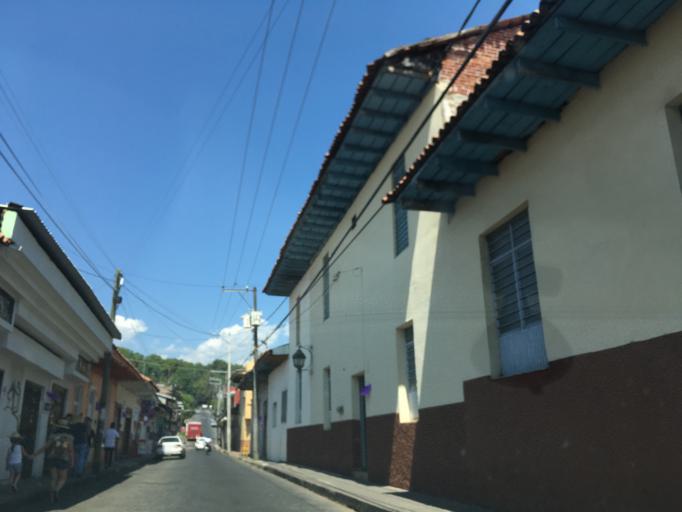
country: MX
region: Michoacan
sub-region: Uruapan
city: Uruapan
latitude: 19.4243
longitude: -102.0675
